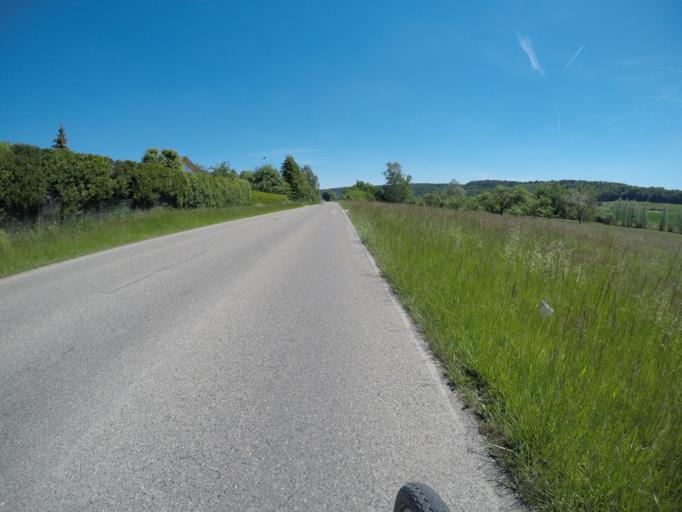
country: DE
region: Baden-Wuerttemberg
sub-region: Regierungsbezirk Stuttgart
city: Magstadt
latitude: 48.7452
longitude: 8.9812
